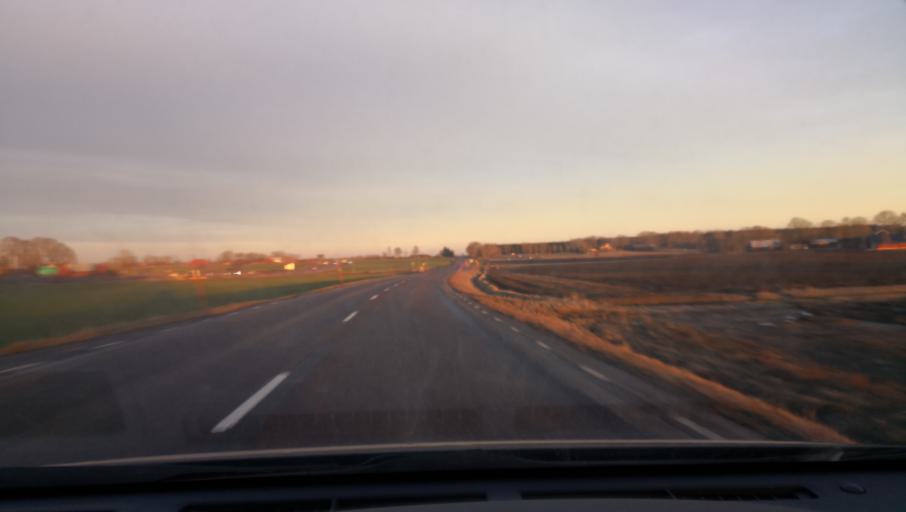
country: SE
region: OErebro
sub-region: Orebro Kommun
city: Vintrosa
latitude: 59.2444
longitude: 14.9546
